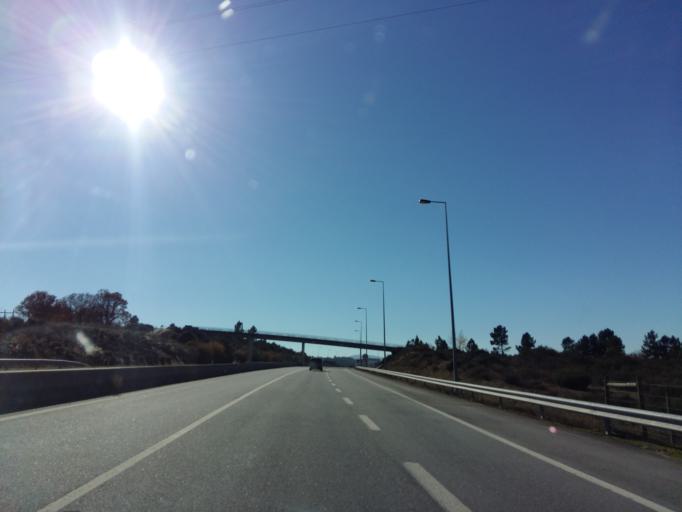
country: PT
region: Castelo Branco
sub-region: Covilha
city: Covilha
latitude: 40.2329
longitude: -7.4846
